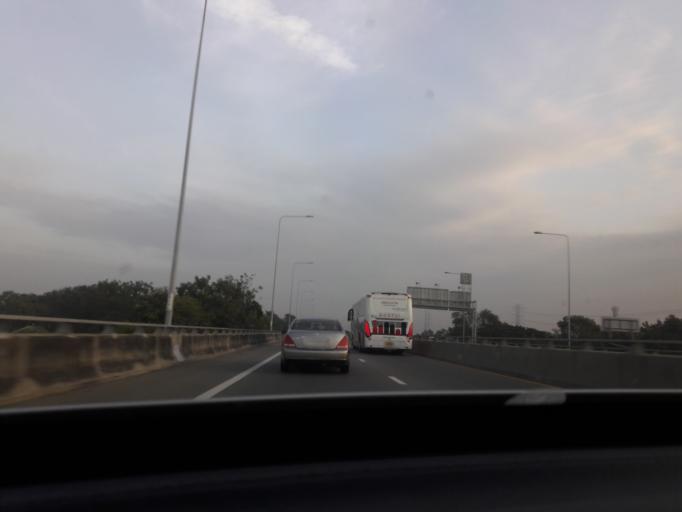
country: TH
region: Bangkok
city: Don Mueang
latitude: 13.9462
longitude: 100.5625
